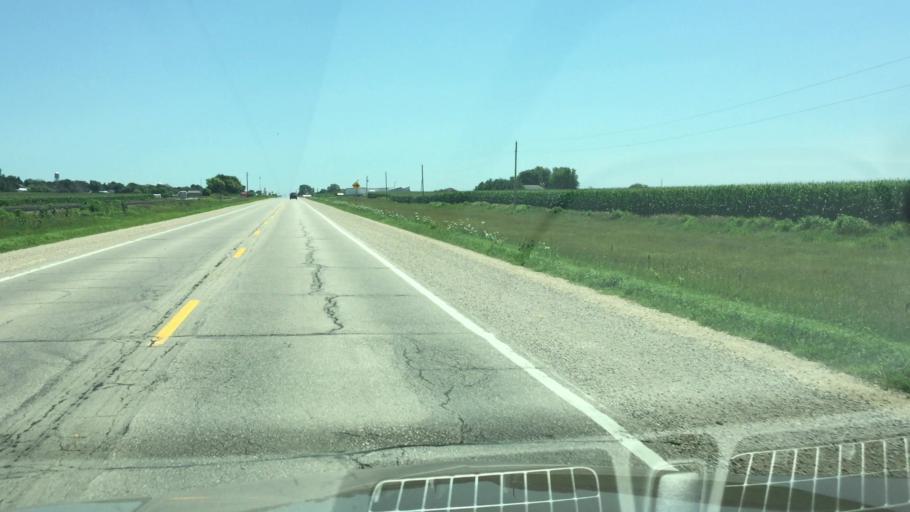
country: US
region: Iowa
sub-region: Cedar County
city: Mechanicsville
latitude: 41.9067
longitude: -91.2729
